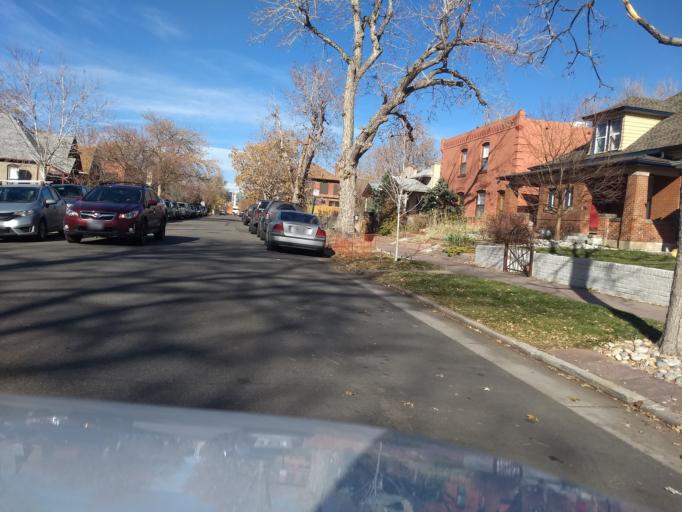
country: US
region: Colorado
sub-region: Denver County
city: Denver
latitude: 39.7215
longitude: -104.9922
